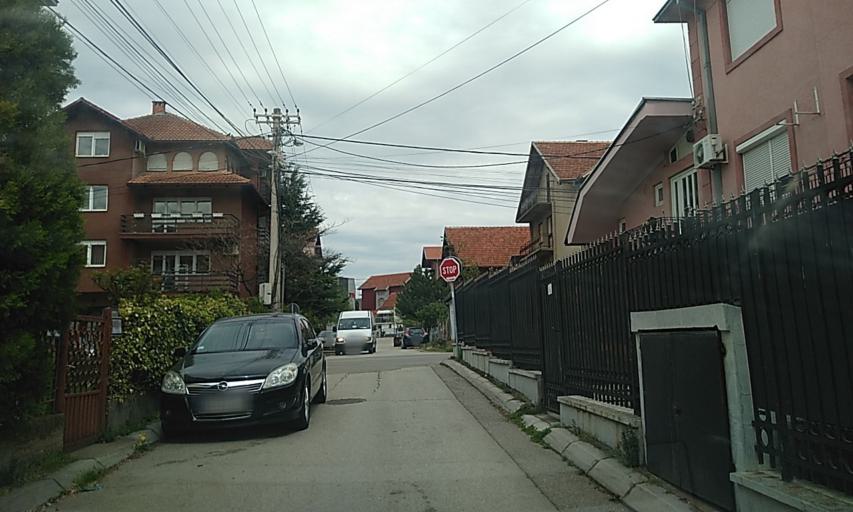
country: RS
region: Central Serbia
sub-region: Nisavski Okrug
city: Nis
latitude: 43.3362
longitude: 21.9145
